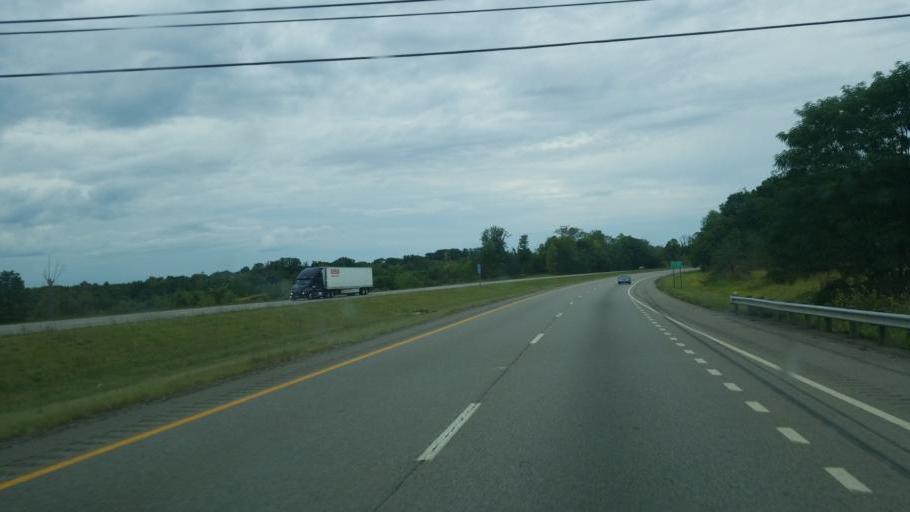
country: US
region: Ohio
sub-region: Trumbull County
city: Churchill
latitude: 41.1600
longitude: -80.6193
